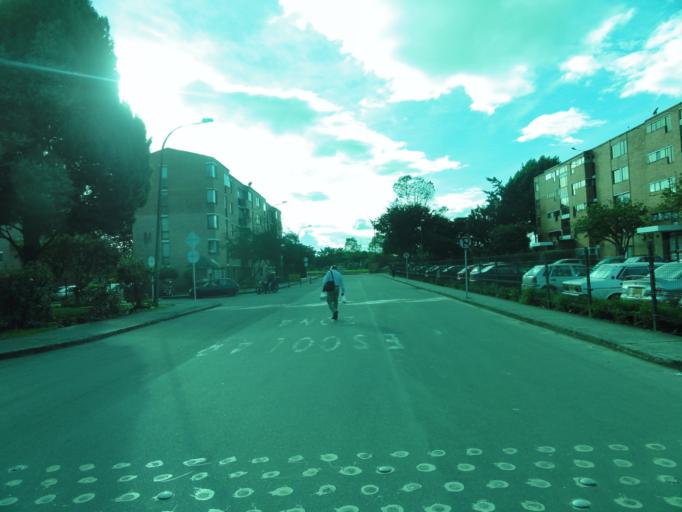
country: CO
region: Bogota D.C.
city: Bogota
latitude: 4.6524
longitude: -74.0903
